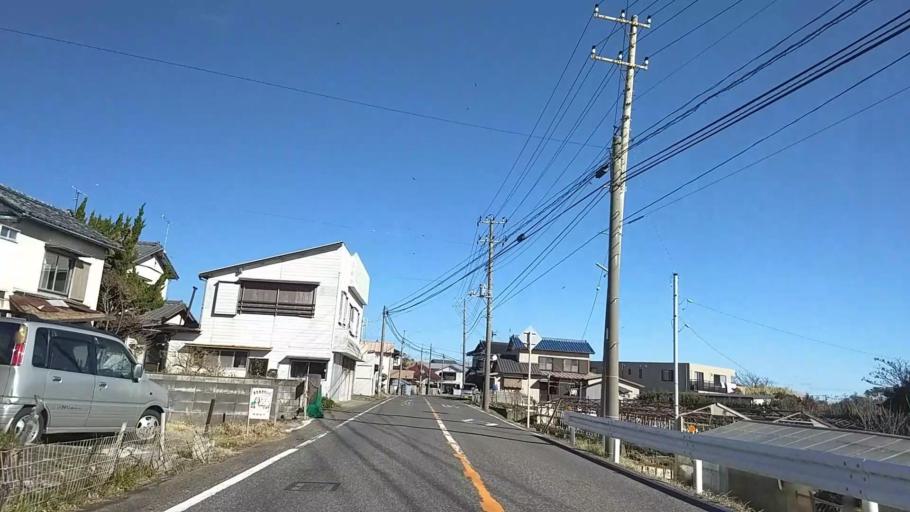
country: JP
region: Chiba
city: Tateyama
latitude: 34.9448
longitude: 139.9610
